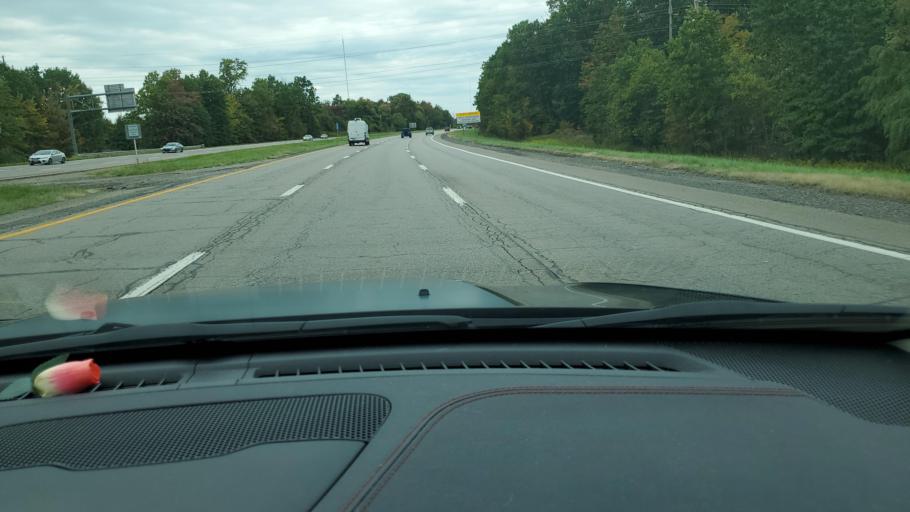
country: US
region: Ohio
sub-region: Mahoning County
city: Poland
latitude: 41.0314
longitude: -80.6295
